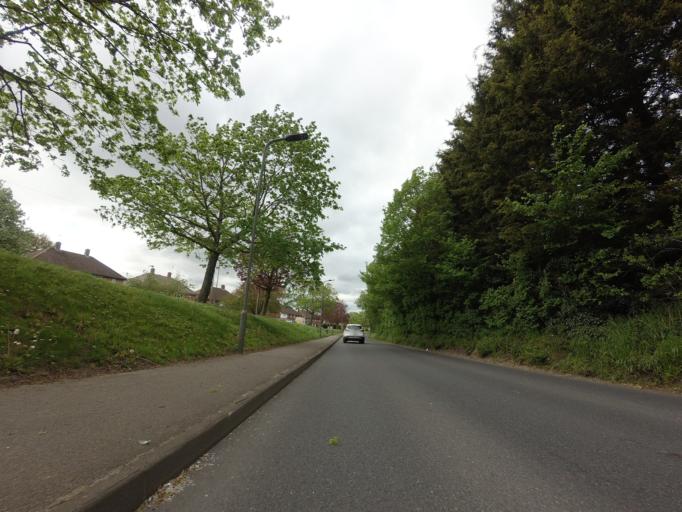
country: GB
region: England
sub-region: Greater London
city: Orpington
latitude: 51.3775
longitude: 0.1223
